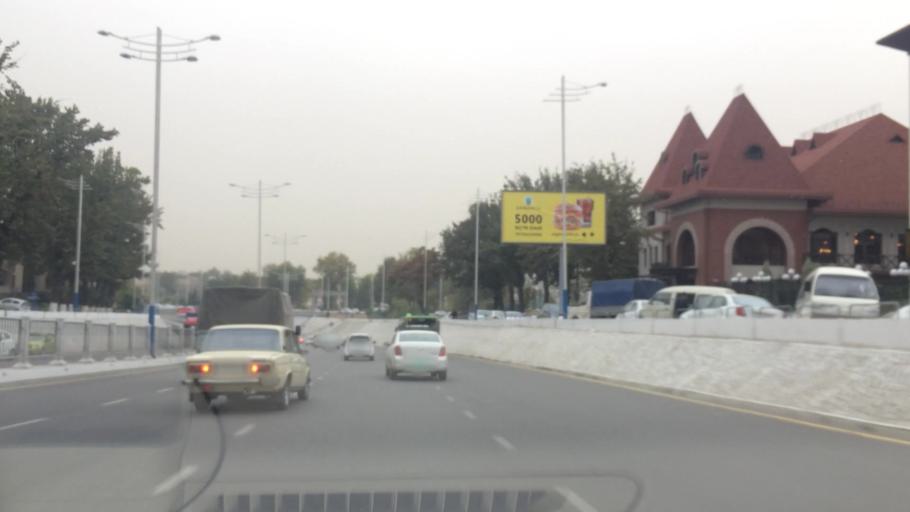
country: UZ
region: Toshkent Shahri
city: Tashkent
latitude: 41.3064
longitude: 69.3050
